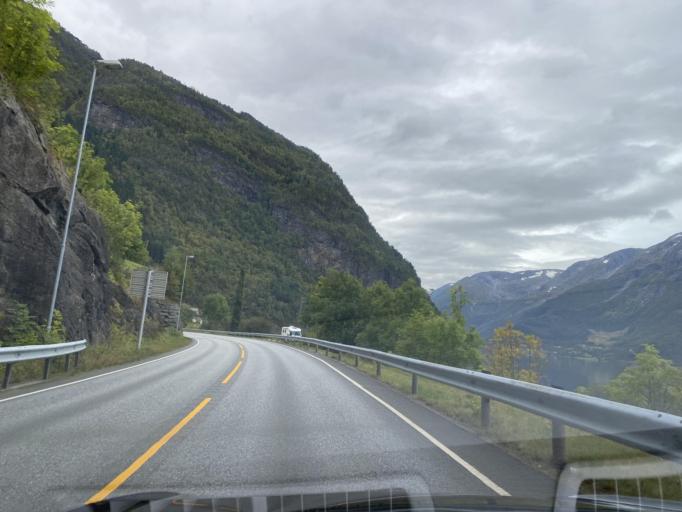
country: NO
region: Hordaland
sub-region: Odda
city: Odda
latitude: 60.1888
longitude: 6.5890
